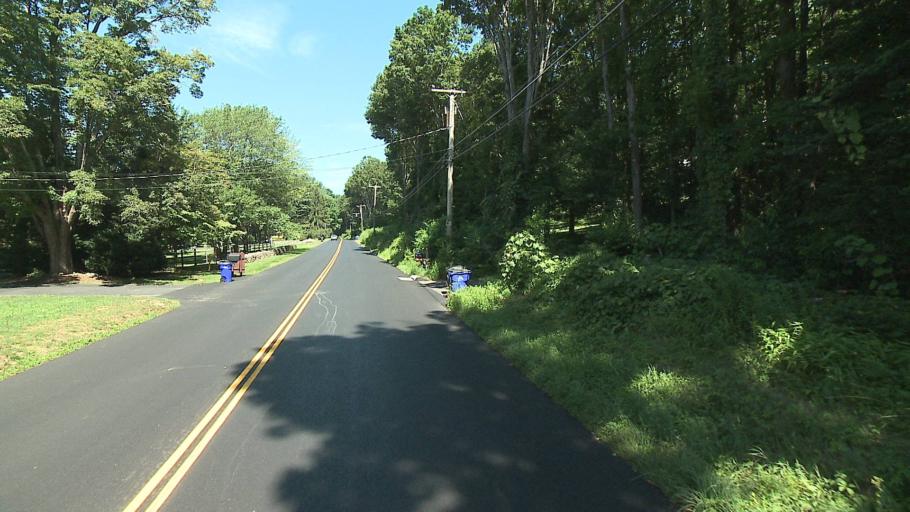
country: US
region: Connecticut
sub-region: Hartford County
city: West Simsbury
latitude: 41.9023
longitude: -72.8932
